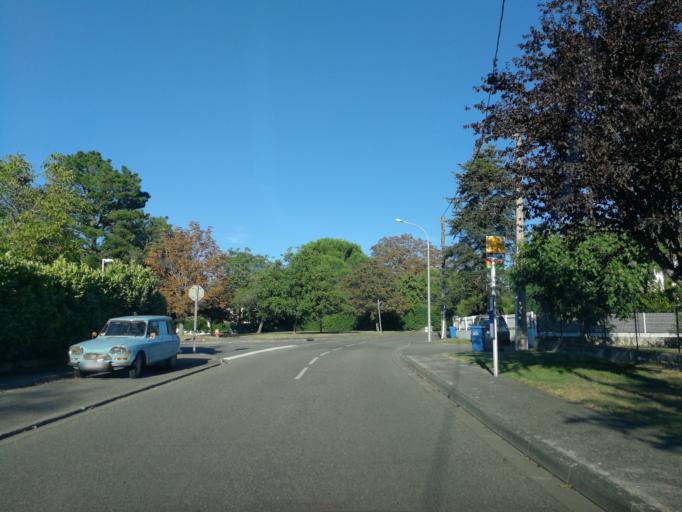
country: FR
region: Midi-Pyrenees
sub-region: Departement de la Haute-Garonne
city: Balma
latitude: 43.6160
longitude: 1.5061
